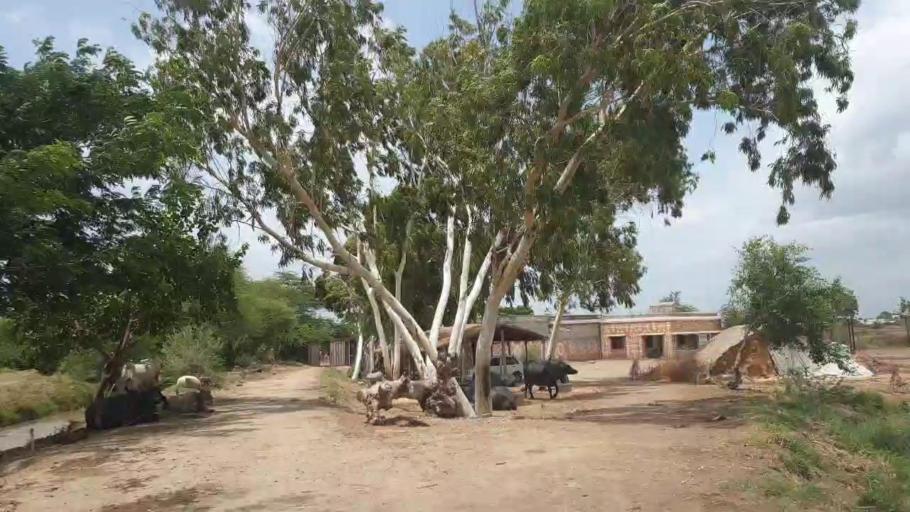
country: PK
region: Sindh
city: Badin
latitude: 24.6638
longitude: 68.9447
